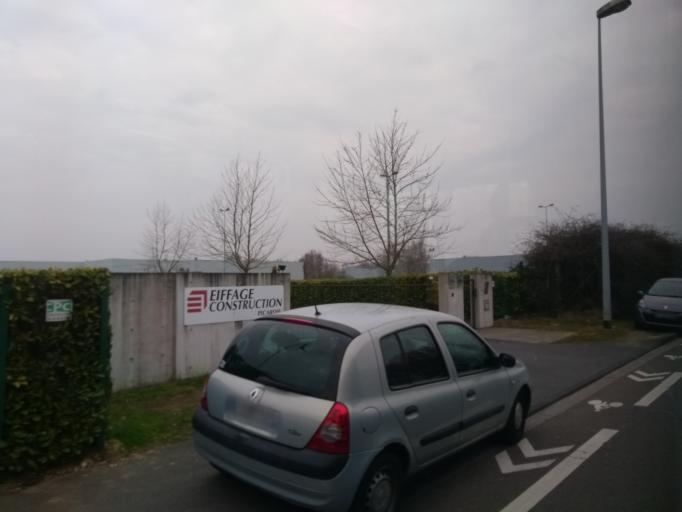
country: FR
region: Picardie
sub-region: Departement de l'Oise
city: Jaux
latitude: 49.3883
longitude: 2.7937
